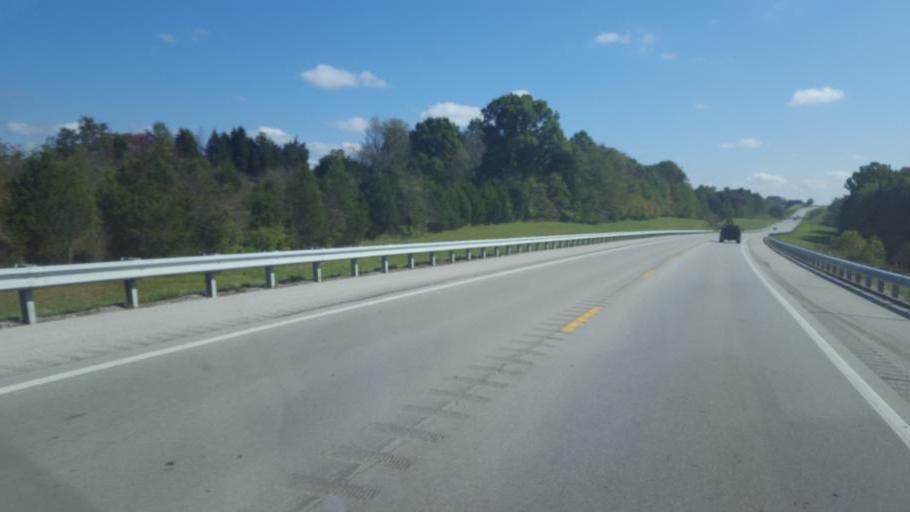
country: US
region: Kentucky
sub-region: Mason County
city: Maysville
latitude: 38.5820
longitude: -83.6759
